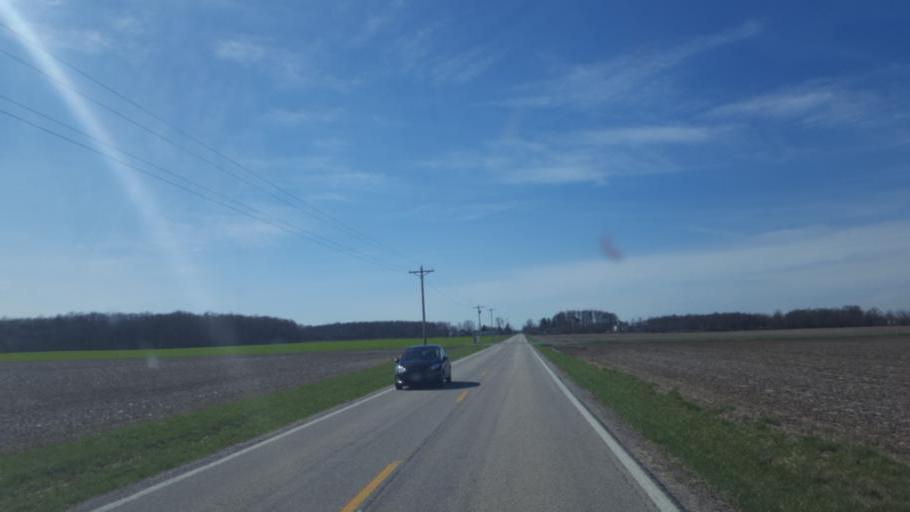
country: US
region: Ohio
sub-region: Morrow County
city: Cardington
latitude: 40.5156
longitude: -82.9628
